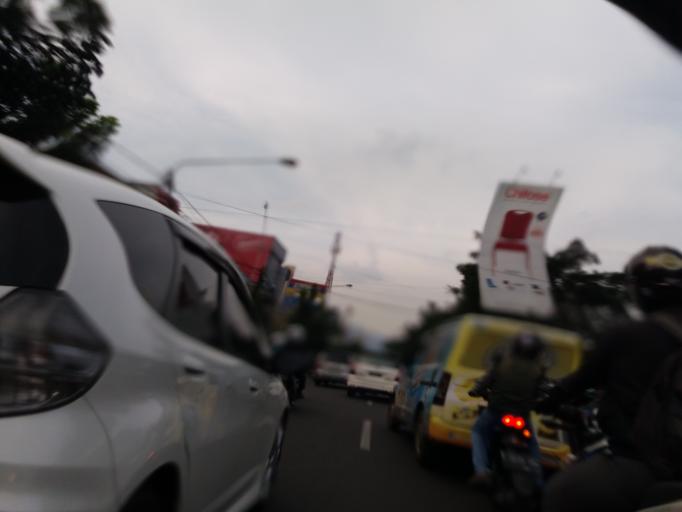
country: ID
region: West Java
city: Bandung
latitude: -6.9120
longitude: 107.6372
